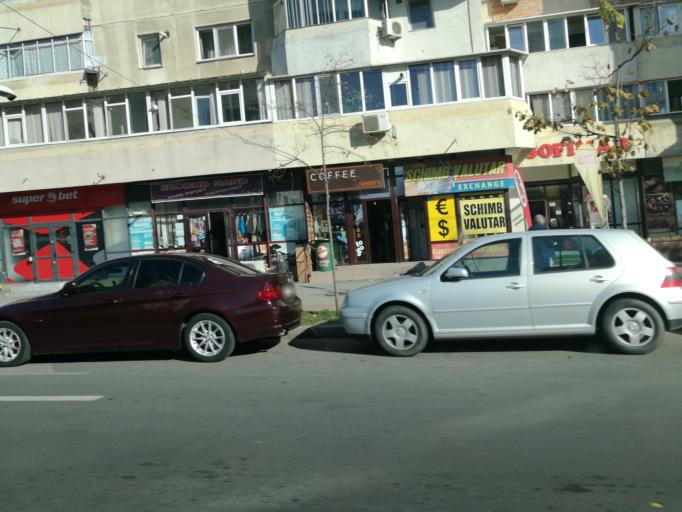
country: RO
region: Iasi
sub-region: Comuna Miroslava
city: Miroslava
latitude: 47.1749
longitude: 27.5443
